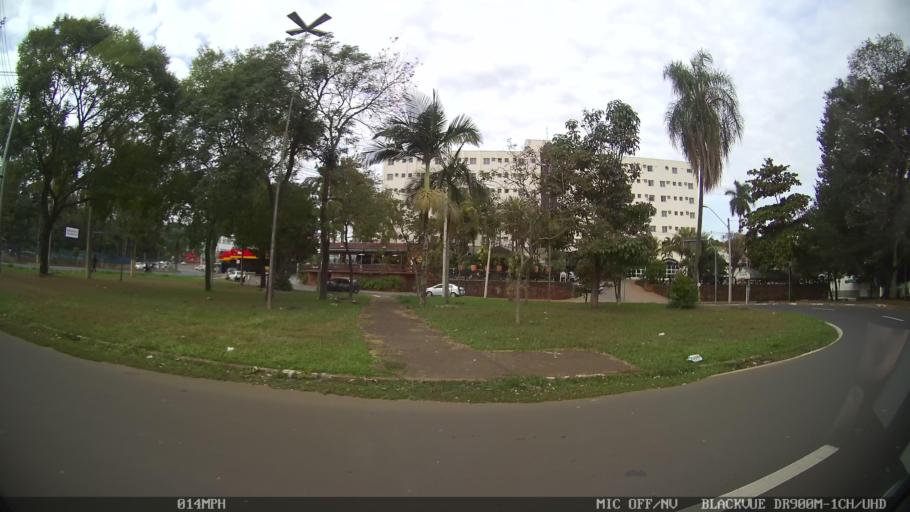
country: BR
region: Sao Paulo
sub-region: Piracicaba
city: Piracicaba
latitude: -22.7151
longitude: -47.6501
